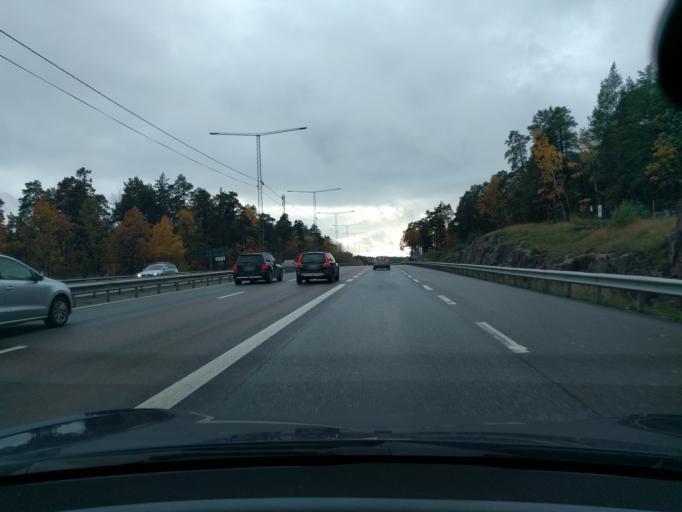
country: SE
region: Stockholm
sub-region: Taby Kommun
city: Taby
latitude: 59.4422
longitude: 18.0929
